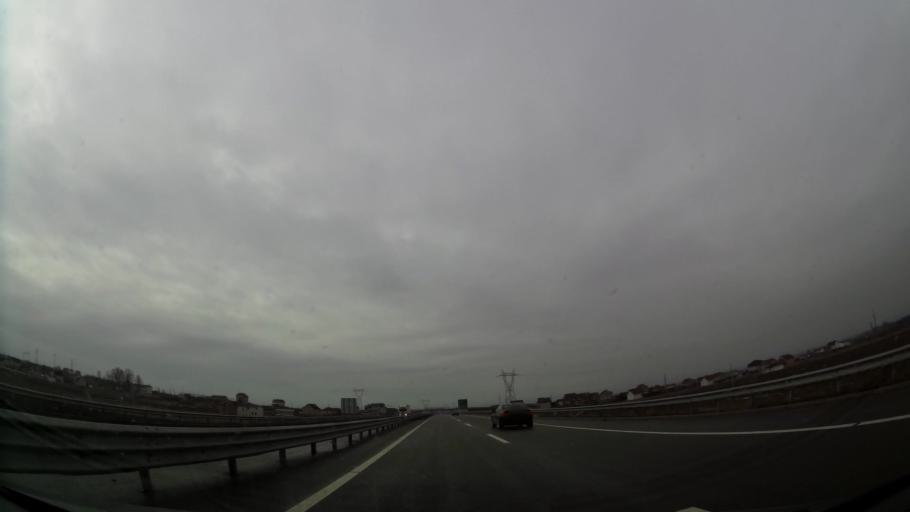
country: XK
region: Pristina
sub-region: Lipjan
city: Lipljan
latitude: 42.4750
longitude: 21.1827
